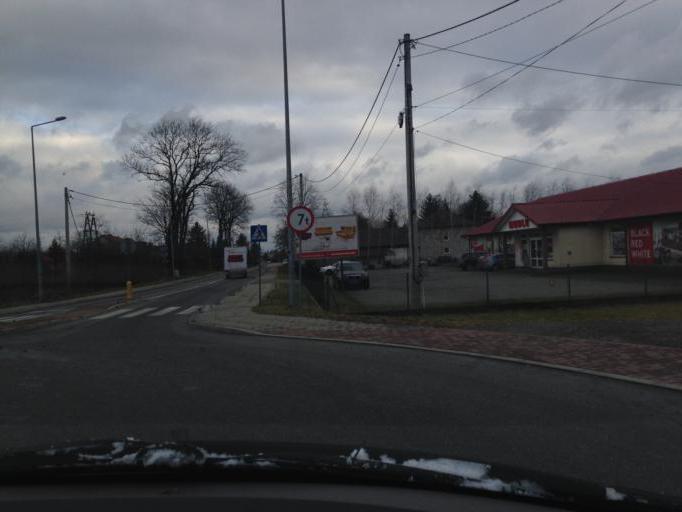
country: PL
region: Lesser Poland Voivodeship
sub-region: Powiat wielicki
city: Gdow
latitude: 49.9078
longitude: 20.1825
